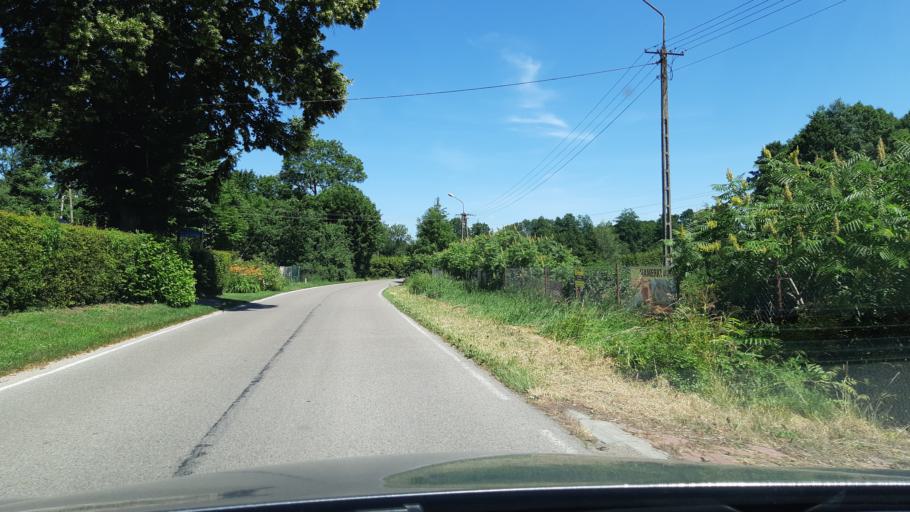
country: PL
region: Warmian-Masurian Voivodeship
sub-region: Powiat gizycki
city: Gizycko
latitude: 53.9173
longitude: 21.6882
